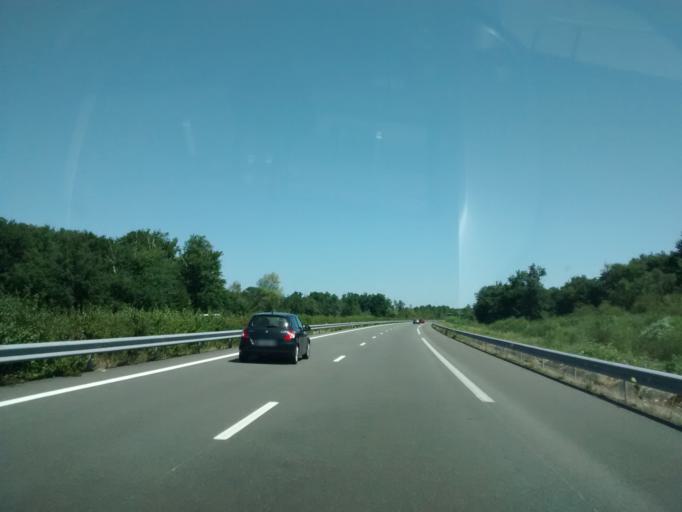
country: FR
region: Aquitaine
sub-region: Departement de la Dordogne
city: Menesplet
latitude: 44.9897
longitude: 0.1017
